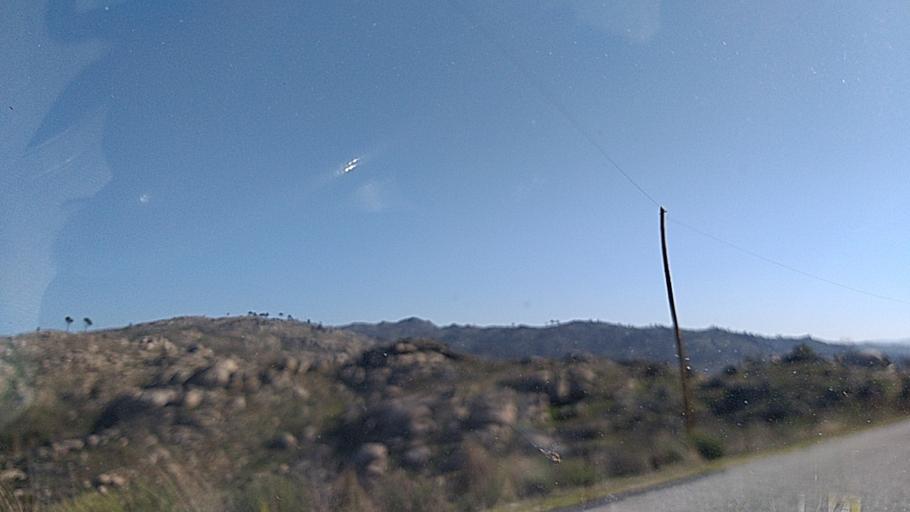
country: PT
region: Guarda
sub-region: Celorico da Beira
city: Celorico da Beira
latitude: 40.6908
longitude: -7.4357
